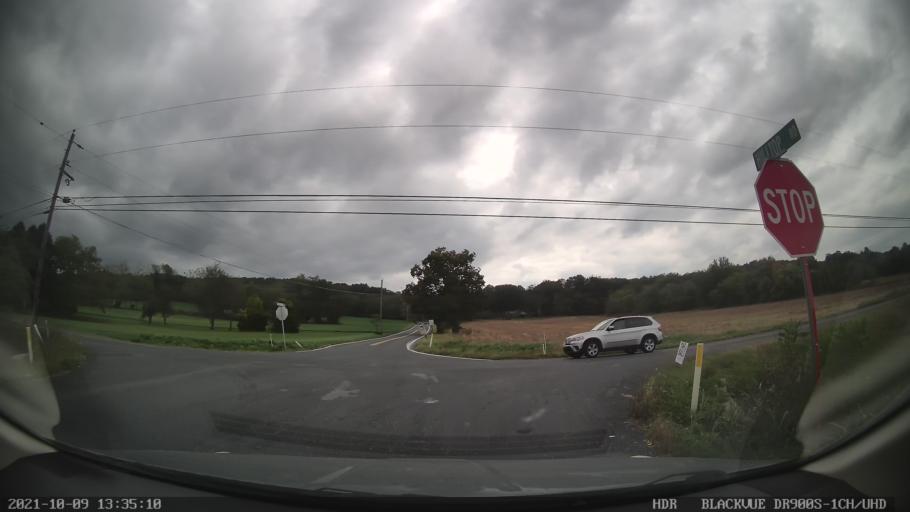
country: US
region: Pennsylvania
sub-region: Lehigh County
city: Alburtis
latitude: 40.5034
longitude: -75.6271
